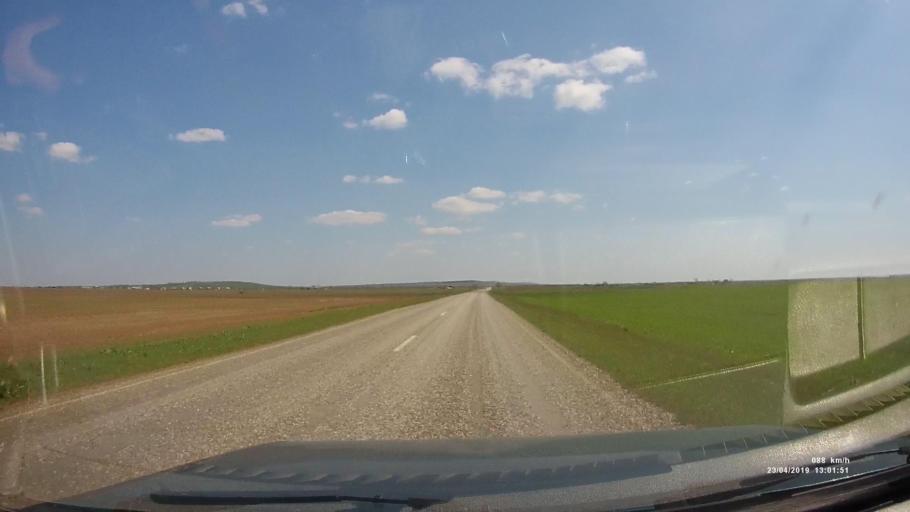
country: RU
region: Kalmykiya
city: Yashalta
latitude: 46.6030
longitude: 42.6602
